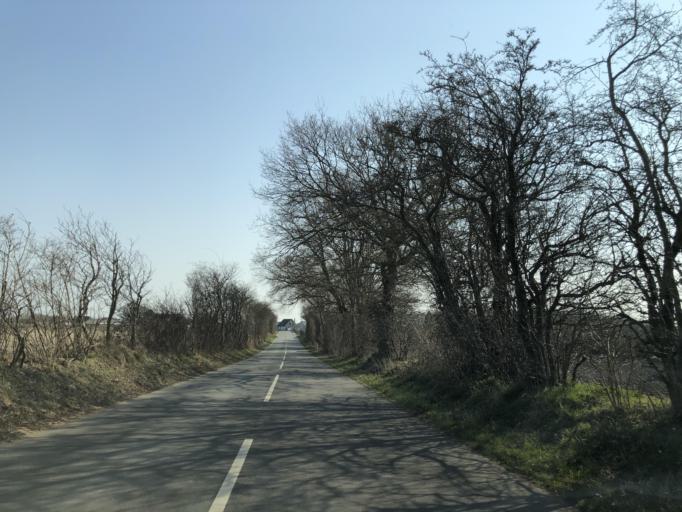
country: DK
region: South Denmark
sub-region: Sonderborg Kommune
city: Nordborg
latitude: 55.0640
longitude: 9.7364
